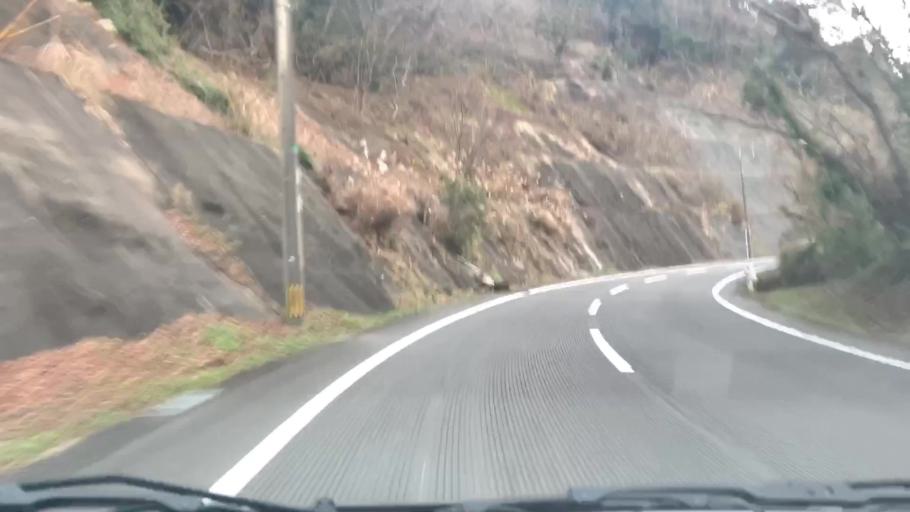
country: JP
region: Saga Prefecture
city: Kashima
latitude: 33.0012
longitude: 130.0637
